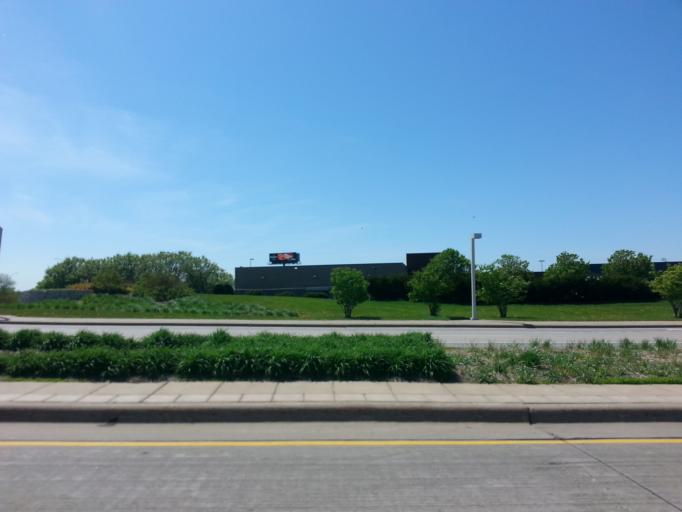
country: US
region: Minnesota
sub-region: Hennepin County
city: Richfield
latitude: 44.8635
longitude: -93.2376
